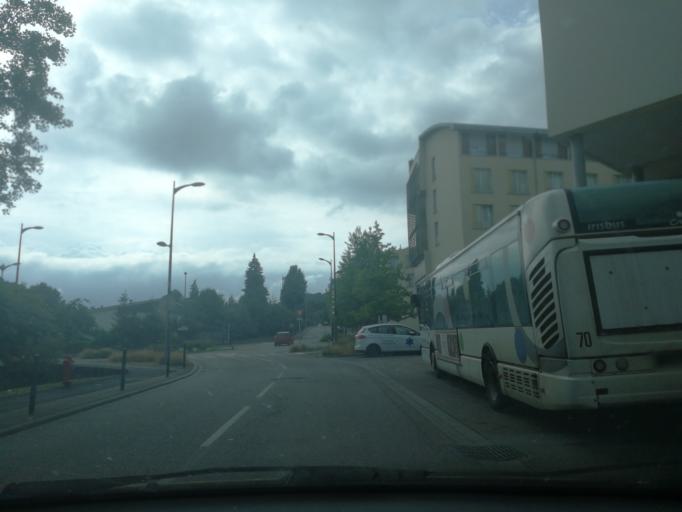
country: FR
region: Lorraine
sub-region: Departement de la Moselle
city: Thionville
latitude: 49.3716
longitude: 6.1508
